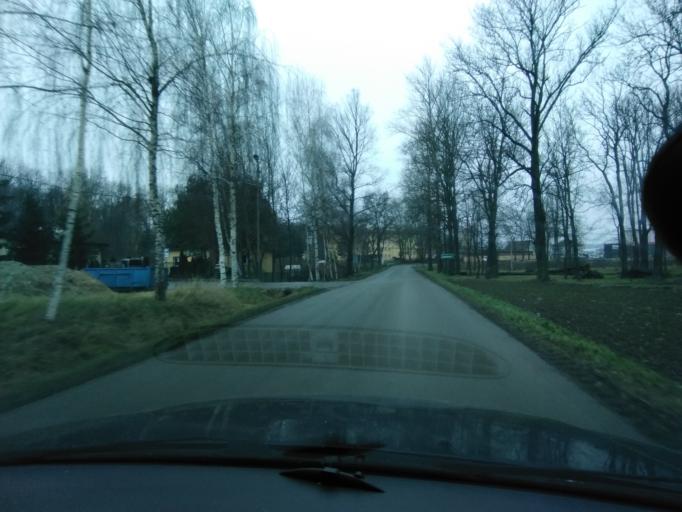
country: PL
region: Subcarpathian Voivodeship
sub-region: Powiat przeworski
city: Zarzecze
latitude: 49.9848
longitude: 22.5459
